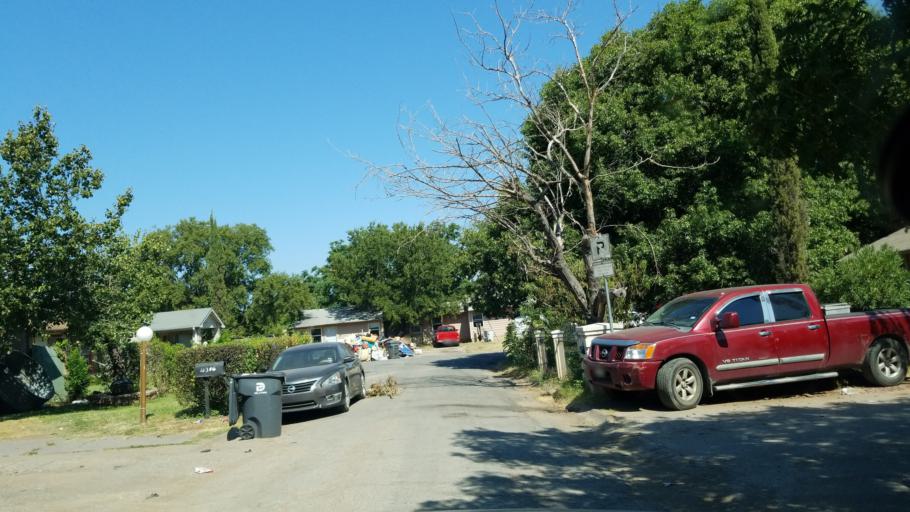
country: US
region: Texas
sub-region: Dallas County
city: Cockrell Hill
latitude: 32.7472
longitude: -96.8904
